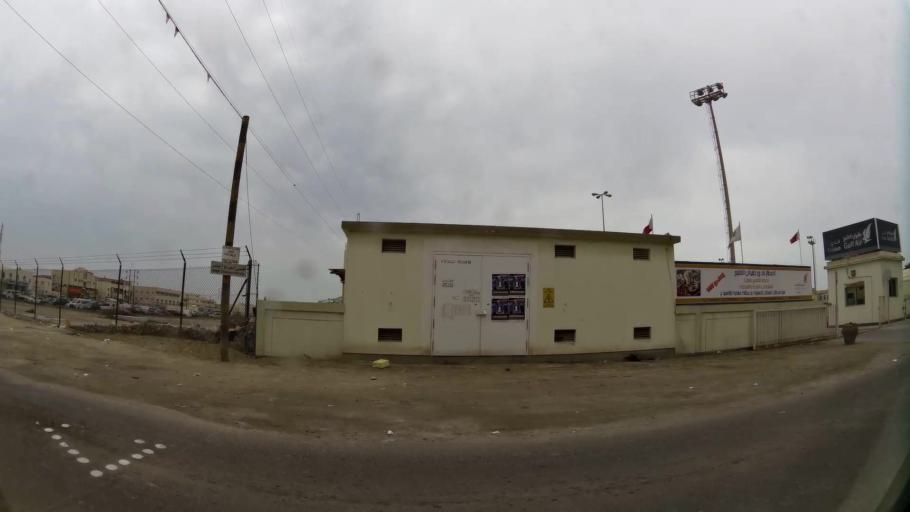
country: BH
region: Northern
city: Madinat `Isa
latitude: 26.1758
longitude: 50.5362
